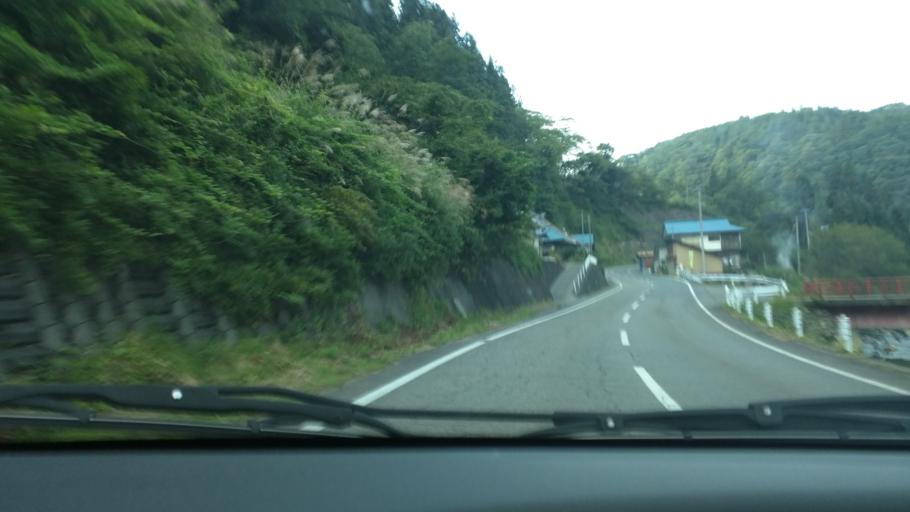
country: JP
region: Fukushima
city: Kitakata
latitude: 37.4615
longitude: 139.6954
